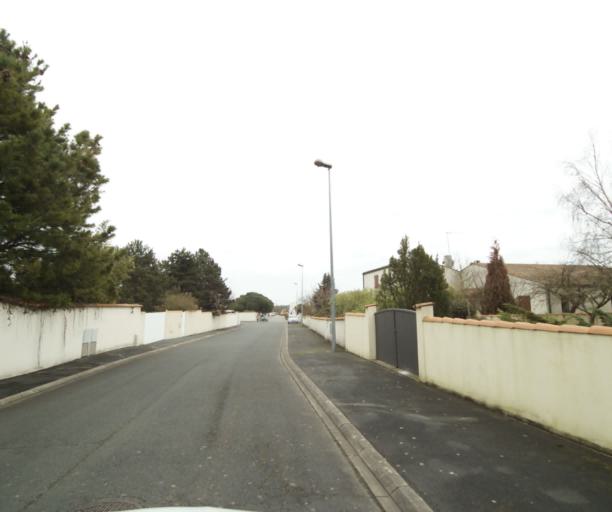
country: FR
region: Poitou-Charentes
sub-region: Departement de la Charente-Maritime
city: Lagord
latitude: 46.1936
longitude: -1.1524
